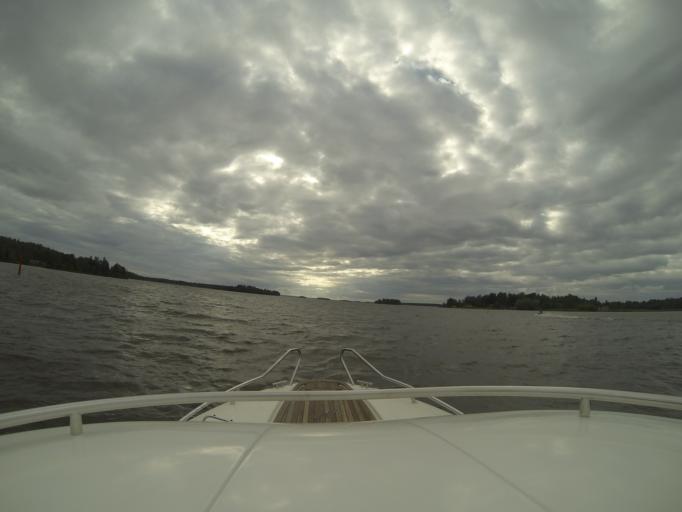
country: SE
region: Soedermanland
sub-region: Eskilstuna Kommun
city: Kvicksund
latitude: 59.4528
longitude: 16.3101
